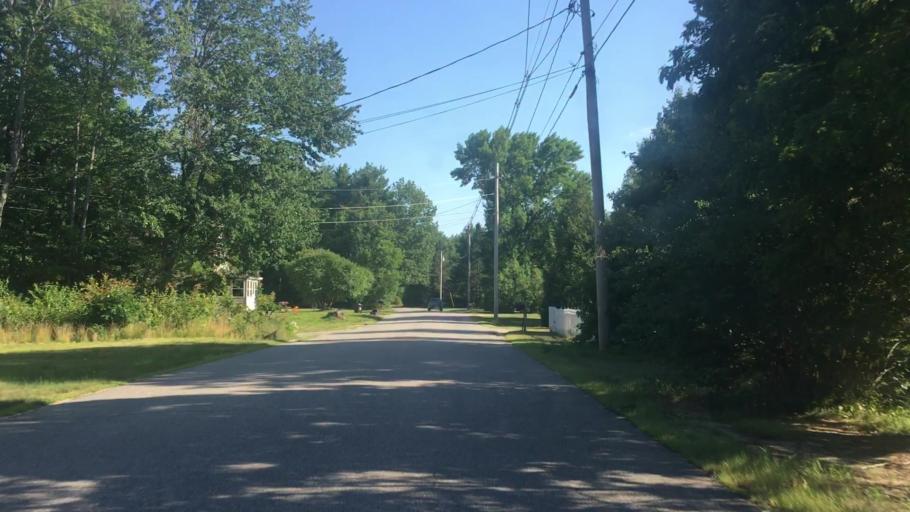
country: US
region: Maine
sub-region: Cumberland County
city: Gorham
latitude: 43.7258
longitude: -70.5161
